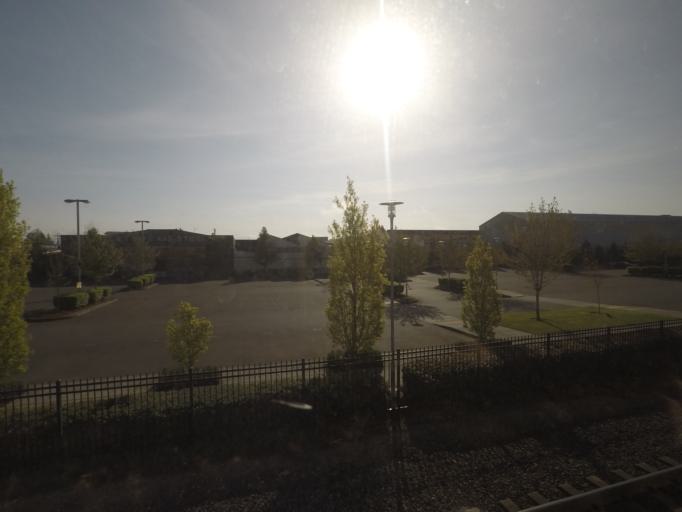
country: US
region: Washington
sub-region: Snohomish County
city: Everett
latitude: 47.9754
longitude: -122.1972
